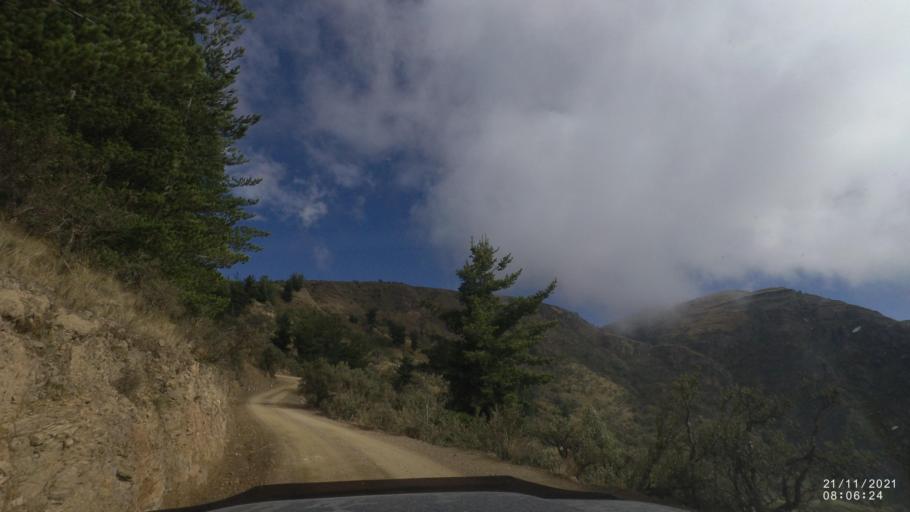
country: BO
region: Cochabamba
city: Cochabamba
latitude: -17.2883
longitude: -66.2094
